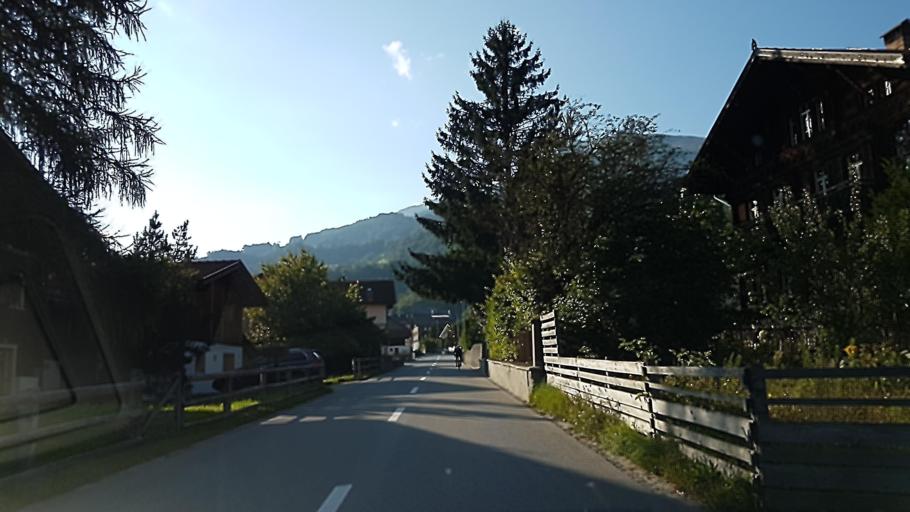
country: CH
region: Grisons
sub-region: Praettigau/Davos District
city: Grusch
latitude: 46.9795
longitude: 9.6534
